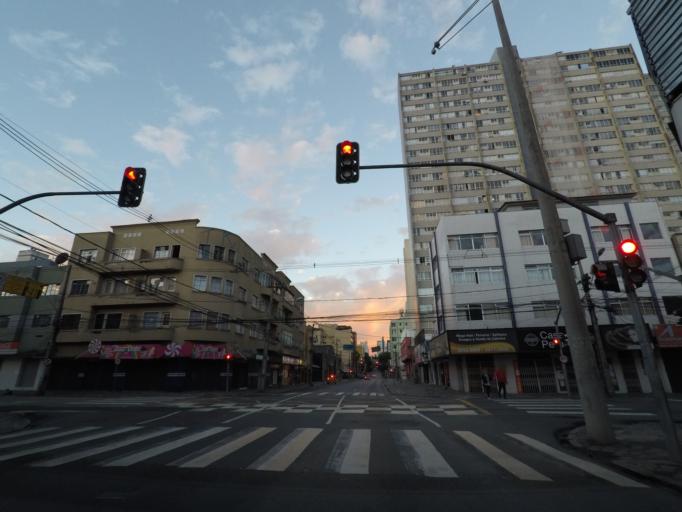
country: BR
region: Parana
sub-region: Curitiba
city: Curitiba
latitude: -25.4329
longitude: -49.2640
